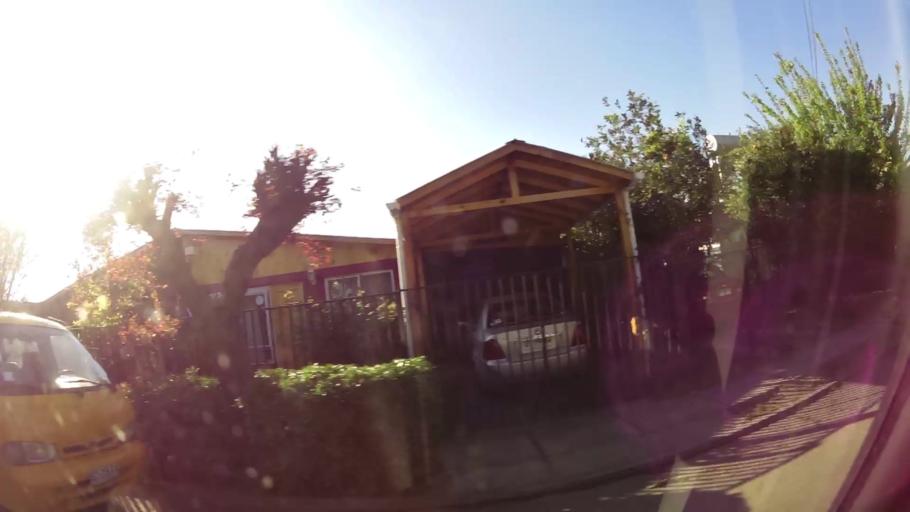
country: CL
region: Santiago Metropolitan
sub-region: Provincia de Santiago
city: Lo Prado
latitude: -33.4872
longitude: -70.7585
